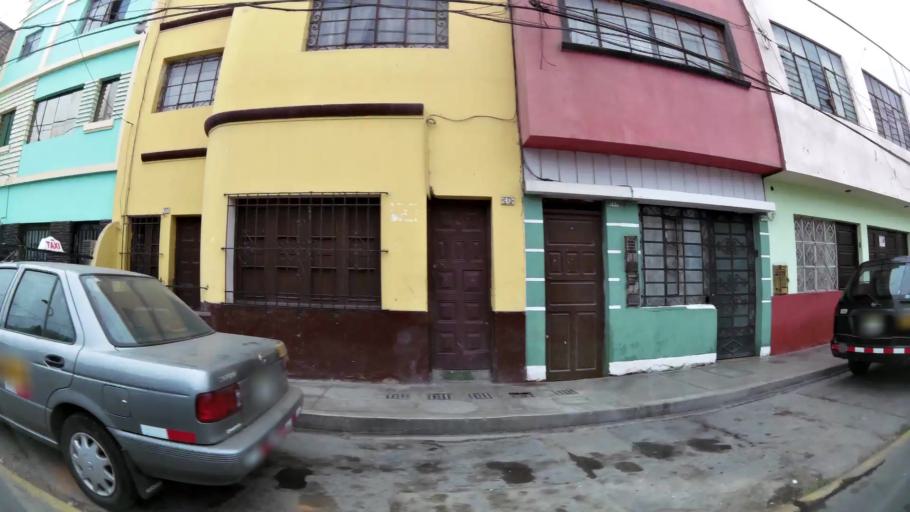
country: PE
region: Callao
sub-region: Callao
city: Callao
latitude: -12.0531
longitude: -77.1362
